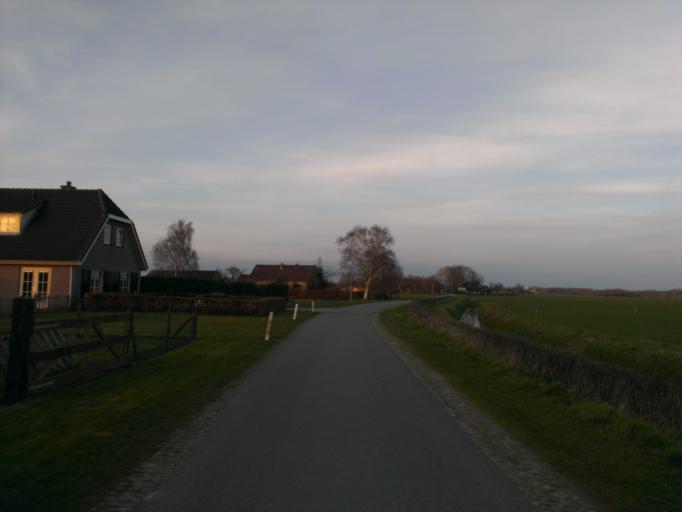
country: NL
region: Overijssel
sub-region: Gemeente Olst-Wijhe
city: Wijhe
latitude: 52.3908
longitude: 6.1059
